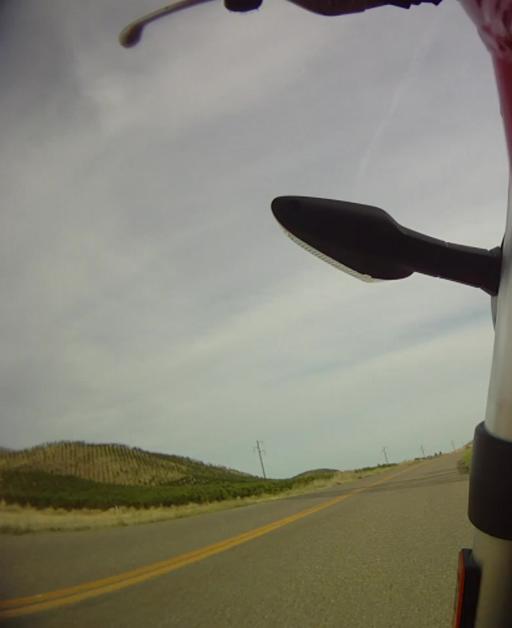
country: US
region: California
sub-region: Stanislaus County
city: Patterson
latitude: 37.4797
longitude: -121.2102
